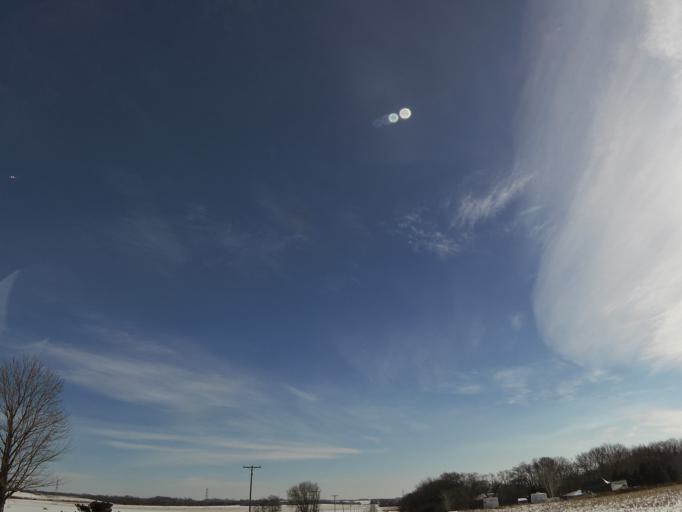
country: US
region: Minnesota
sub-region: Dakota County
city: Rosemount
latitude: 44.7389
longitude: -93.0231
